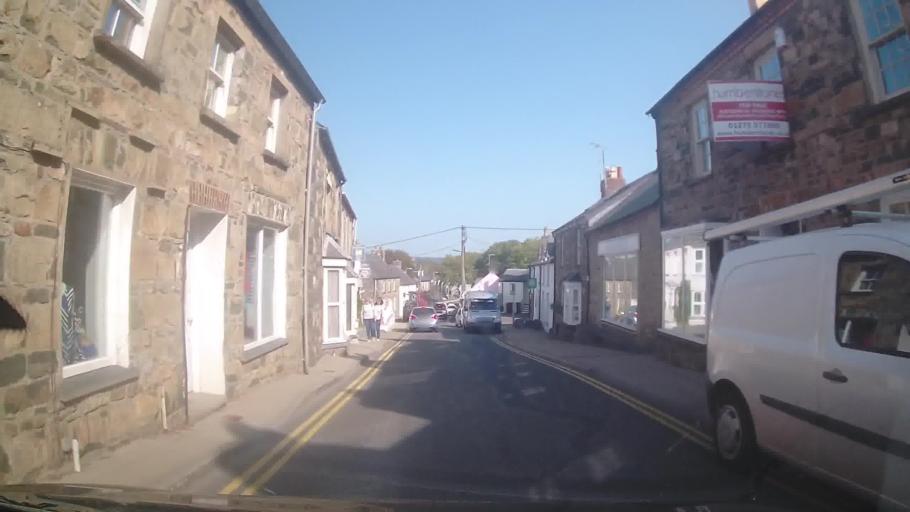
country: GB
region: Wales
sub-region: Pembrokeshire
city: Newport
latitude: 52.0163
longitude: -4.8322
